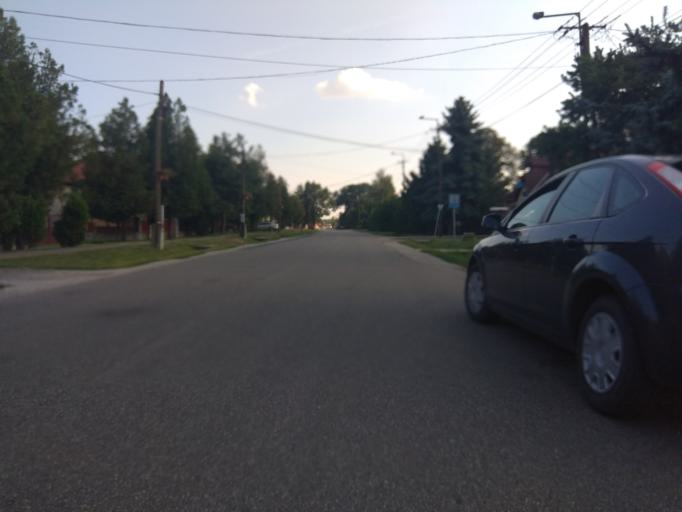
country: HU
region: Borsod-Abauj-Zemplen
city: Mezokeresztes
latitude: 47.8634
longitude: 20.6789
